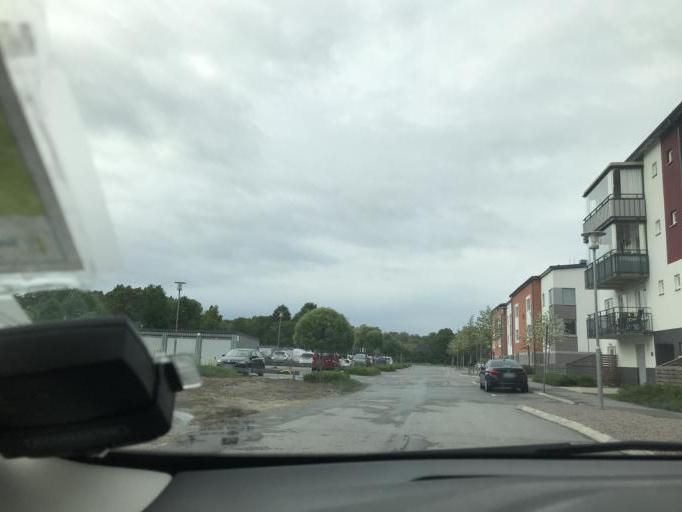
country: SE
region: Stockholm
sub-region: Botkyrka Kommun
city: Tumba
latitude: 59.2013
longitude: 17.8285
